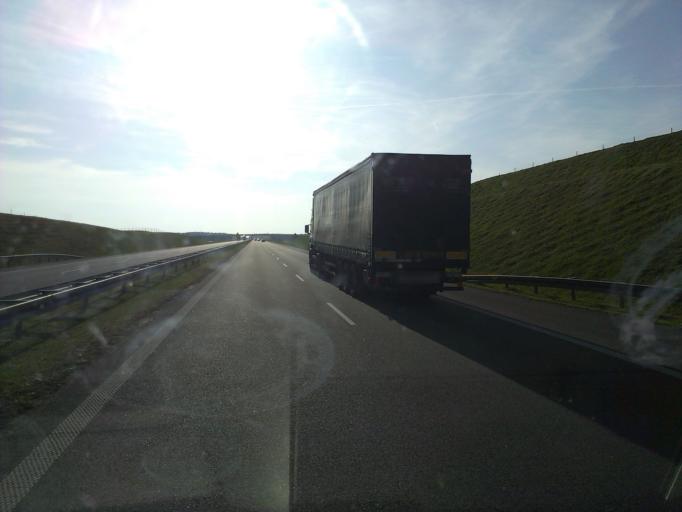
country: PL
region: West Pomeranian Voivodeship
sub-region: Powiat mysliborski
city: Nowogrodek Pomorski
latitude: 52.8887
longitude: 15.0225
